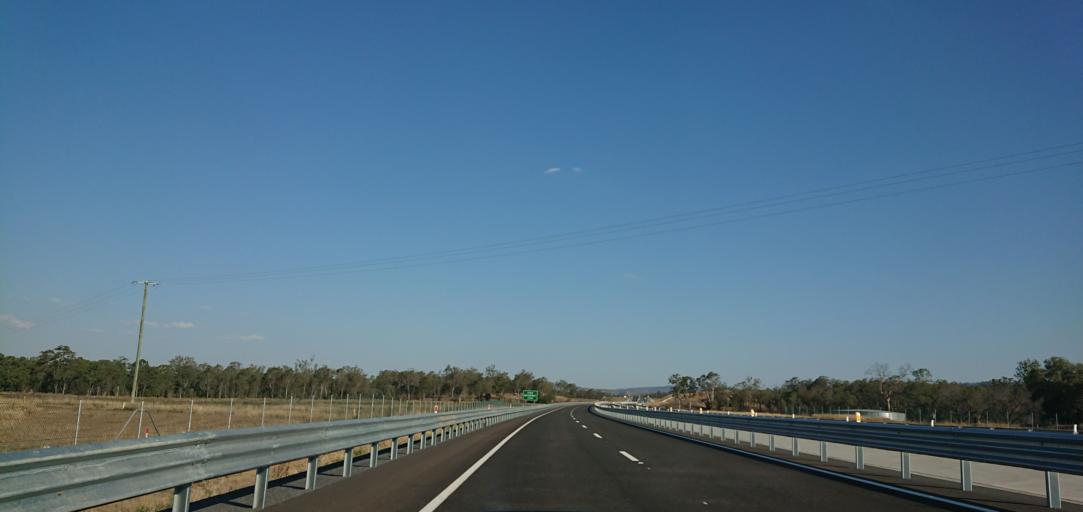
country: AU
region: Queensland
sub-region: Toowoomba
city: Rangeville
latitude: -27.5323
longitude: 152.0744
